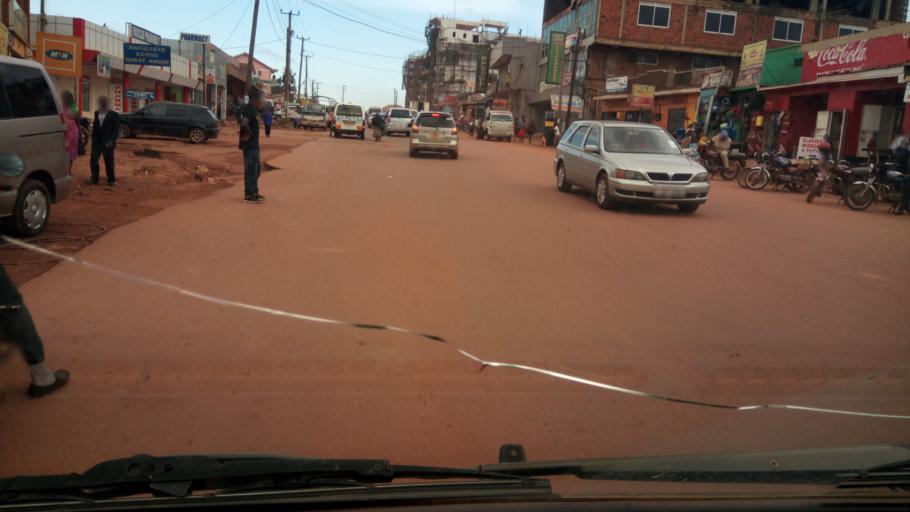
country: UG
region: Central Region
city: Kampala Central Division
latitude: 0.3254
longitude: 32.5589
